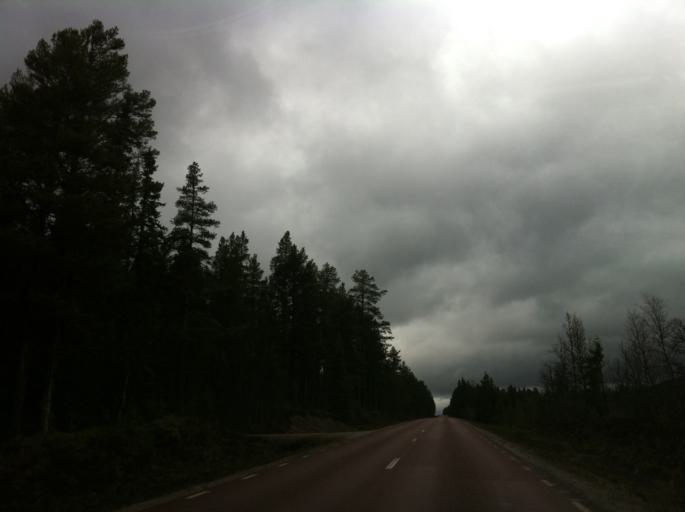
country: NO
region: Hedmark
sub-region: Engerdal
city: Engerdal
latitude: 62.4389
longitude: 12.7138
